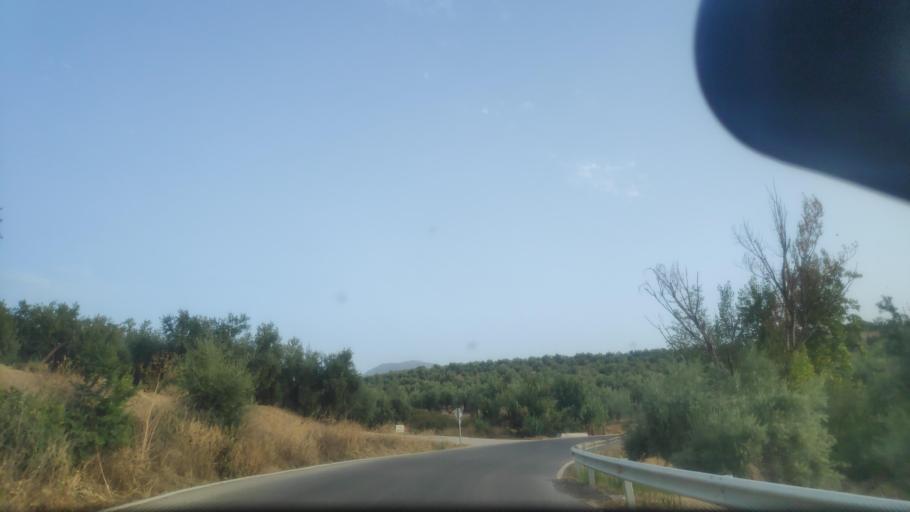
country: ES
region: Andalusia
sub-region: Provincia de Jaen
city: Torres
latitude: 37.8174
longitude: -3.5327
